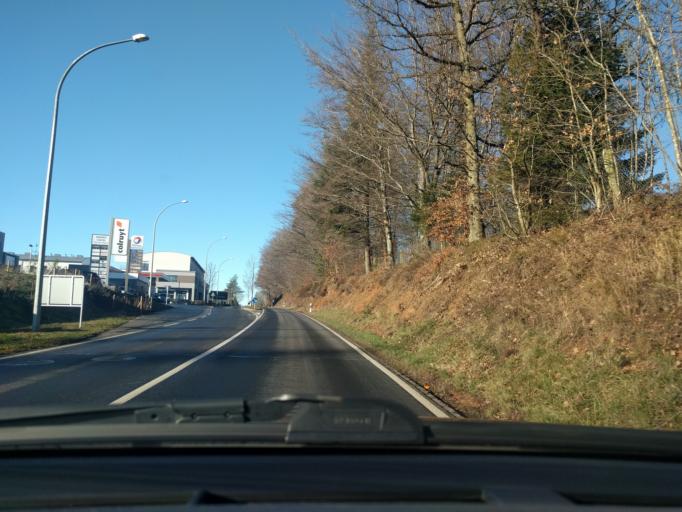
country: LU
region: Diekirch
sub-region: Canton de Clervaux
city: Weiswampach
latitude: 50.1565
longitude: 6.0510
